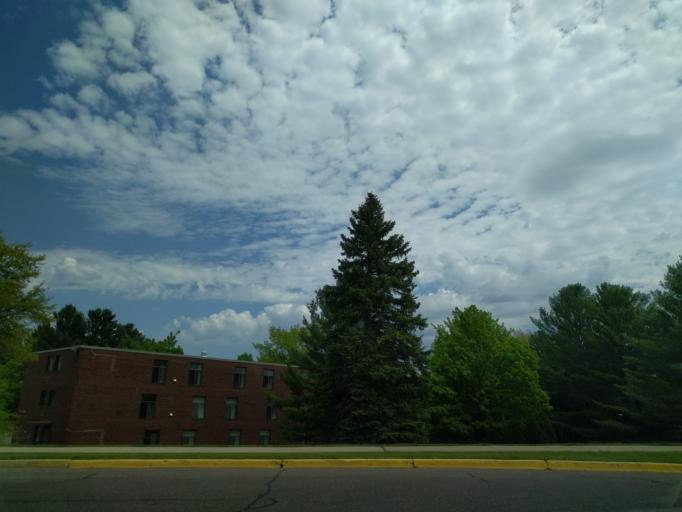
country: US
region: Michigan
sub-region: Marquette County
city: Marquette
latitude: 46.5563
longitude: -87.4035
